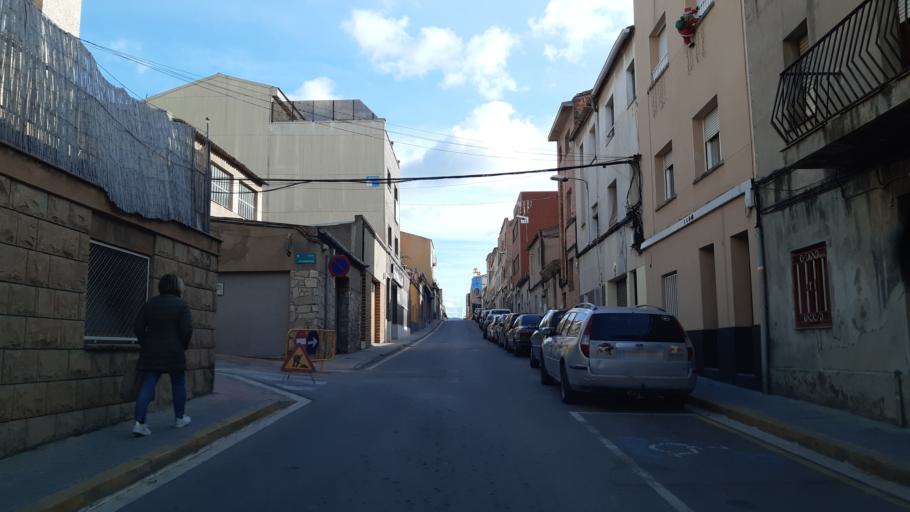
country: ES
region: Catalonia
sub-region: Provincia de Barcelona
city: Vilanova del Cami
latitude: 41.5709
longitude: 1.6359
